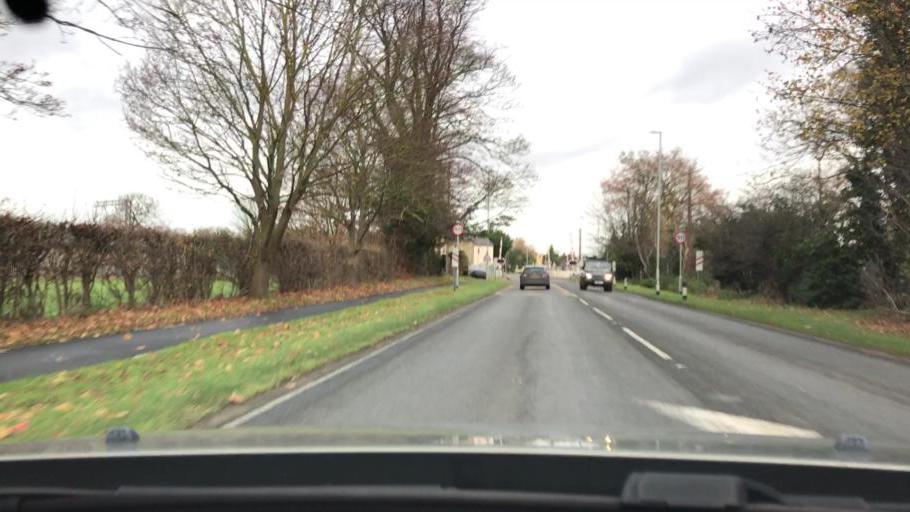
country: GB
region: England
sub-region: Cambridgeshire
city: Harston
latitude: 52.1181
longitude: 0.0548
